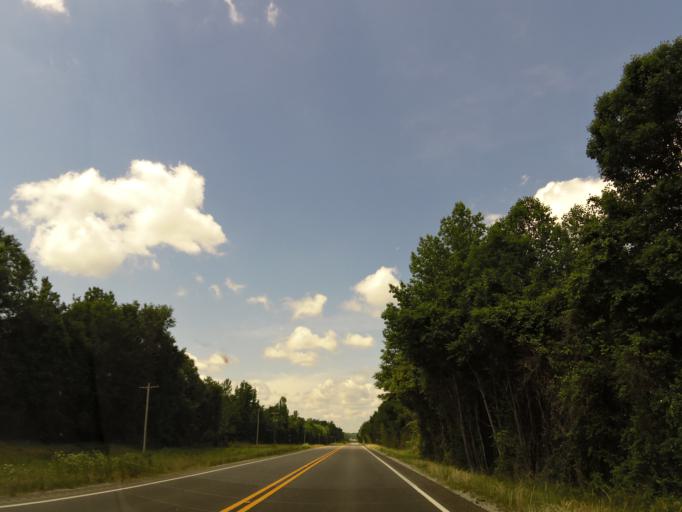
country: US
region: Alabama
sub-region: Marion County
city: Guin
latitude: 33.9491
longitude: -87.9818
